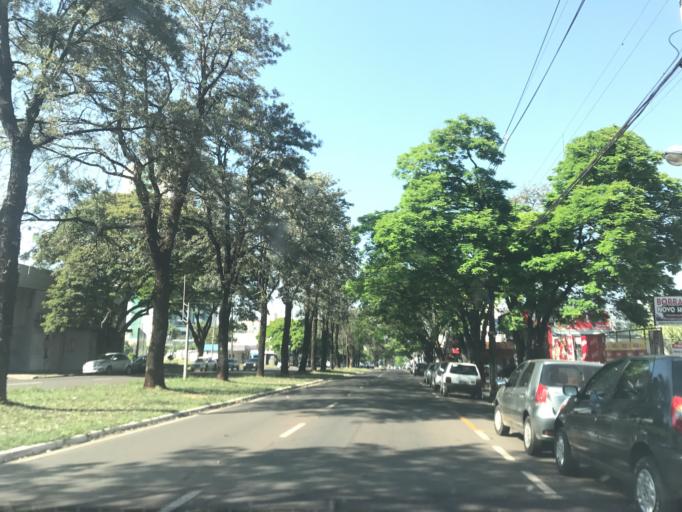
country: BR
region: Parana
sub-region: Maringa
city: Maringa
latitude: -23.4417
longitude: -51.9328
